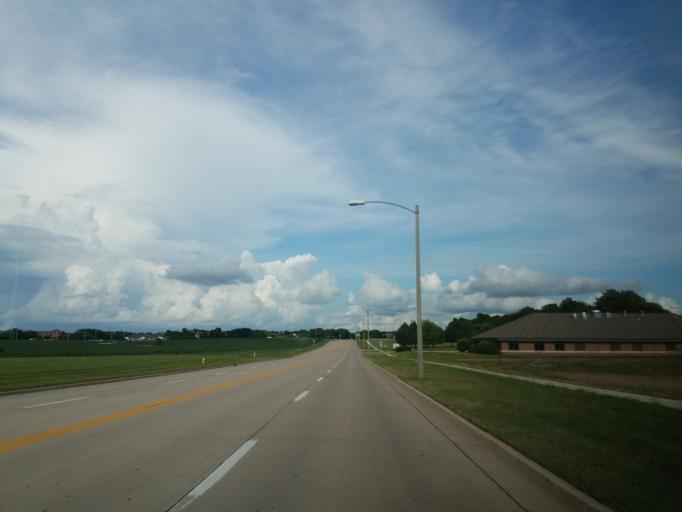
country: US
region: Illinois
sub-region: McLean County
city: Normal
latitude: 40.5075
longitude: -88.9492
